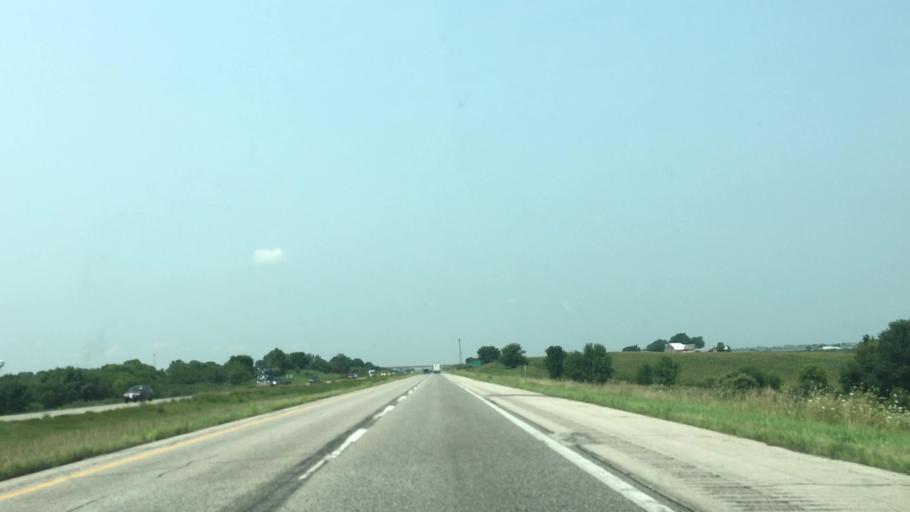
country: US
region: Iowa
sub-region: Benton County
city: Urbana
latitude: 42.2226
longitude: -91.8567
